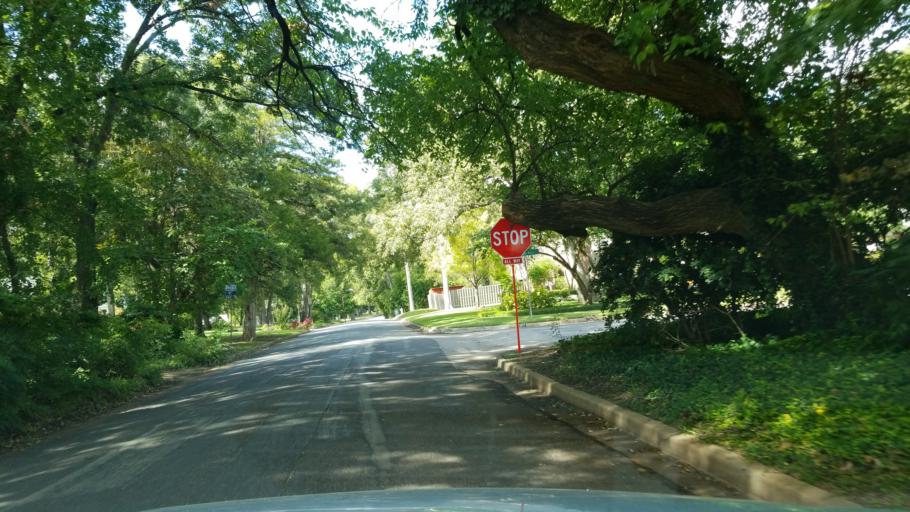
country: US
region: Texas
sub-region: Dallas County
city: Highland Park
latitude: 32.8085
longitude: -96.7195
